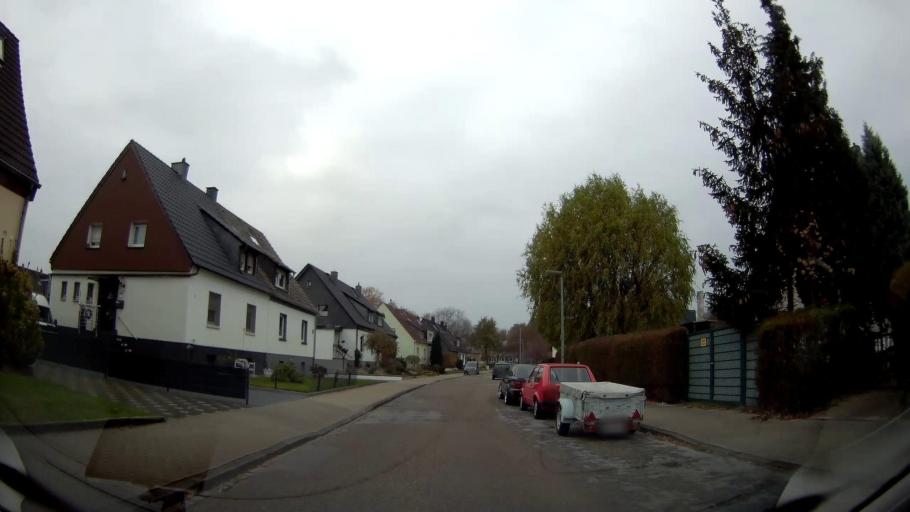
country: DE
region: North Rhine-Westphalia
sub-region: Regierungsbezirk Munster
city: Gladbeck
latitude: 51.5531
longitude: 7.0421
